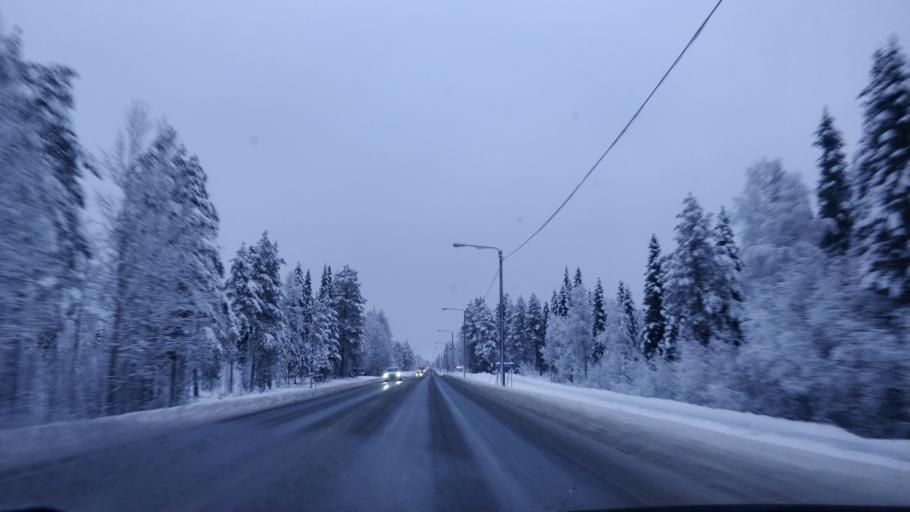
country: FI
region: Lapland
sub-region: Rovaniemi
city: Rovaniemi
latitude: 66.4505
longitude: 25.5727
